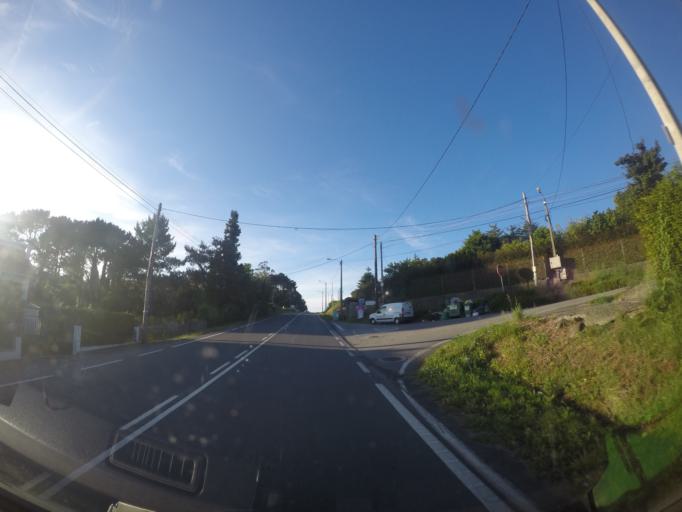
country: ES
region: Galicia
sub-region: Provincia da Coruna
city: Noia
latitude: 42.7705
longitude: -8.9366
